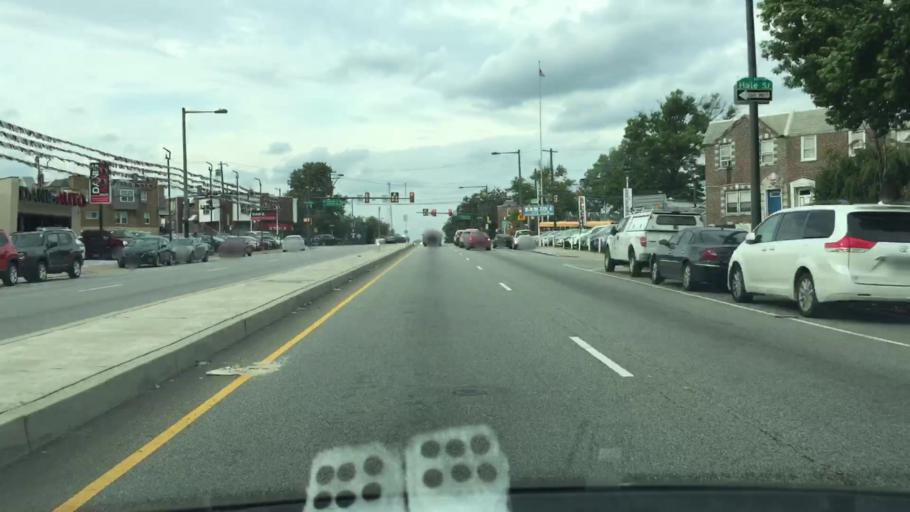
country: US
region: New Jersey
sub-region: Burlington County
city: Palmyra
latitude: 40.0282
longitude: -75.0625
